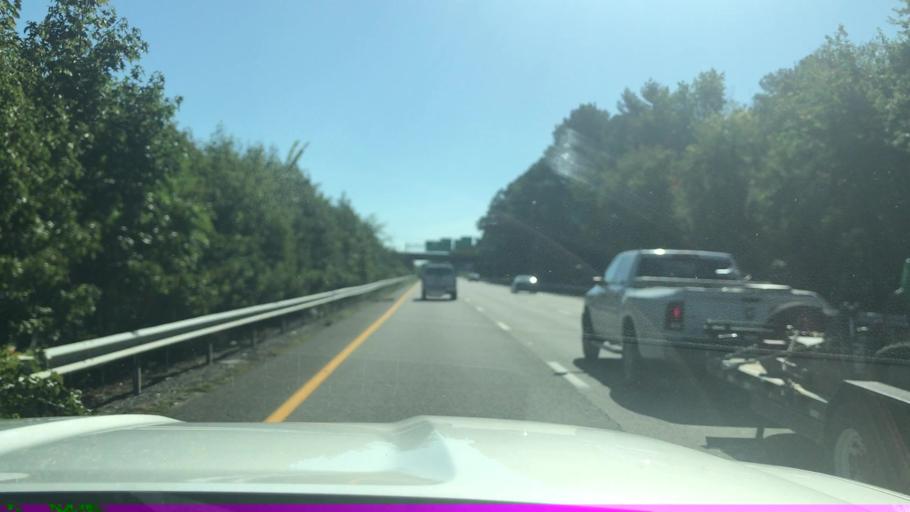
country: US
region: Virginia
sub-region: Henrico County
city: Highland Springs
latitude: 37.5317
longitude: -77.3476
